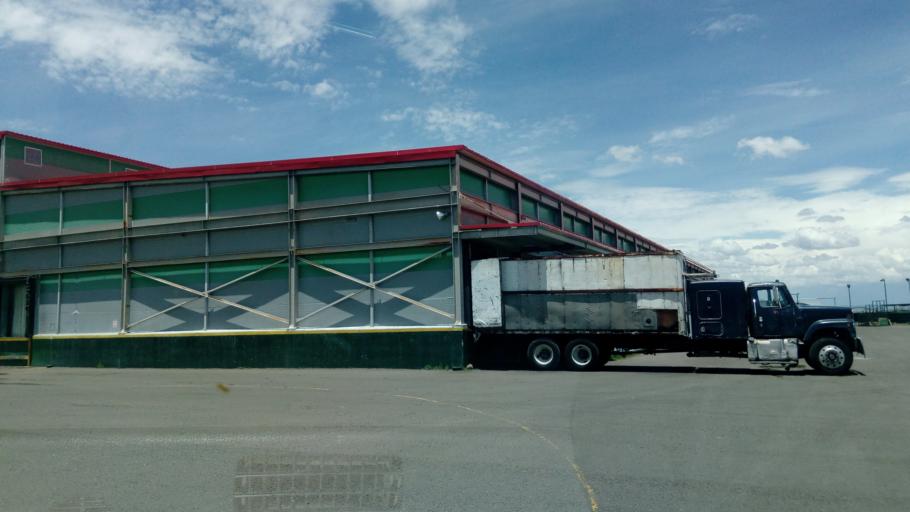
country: MX
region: Durango
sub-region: Durango
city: Jose Refugio Salcido
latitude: 24.1704
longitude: -104.4986
